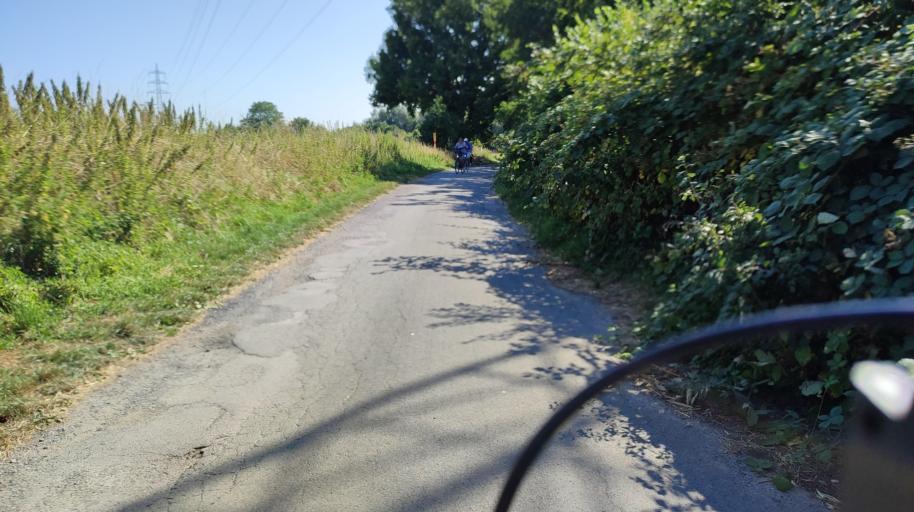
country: DE
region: North Rhine-Westphalia
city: Lanstrop
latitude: 51.6004
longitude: 7.5650
